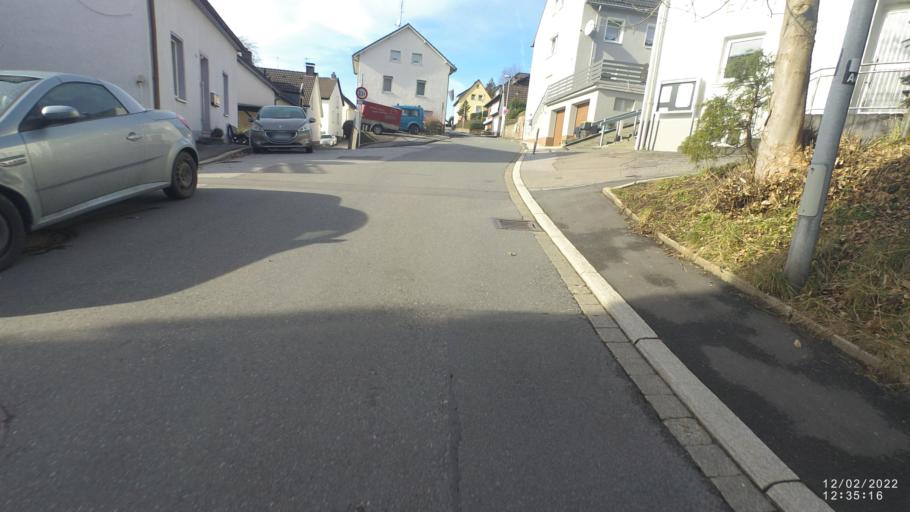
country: DE
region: North Rhine-Westphalia
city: Neuenrade
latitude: 51.3019
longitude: 7.7568
